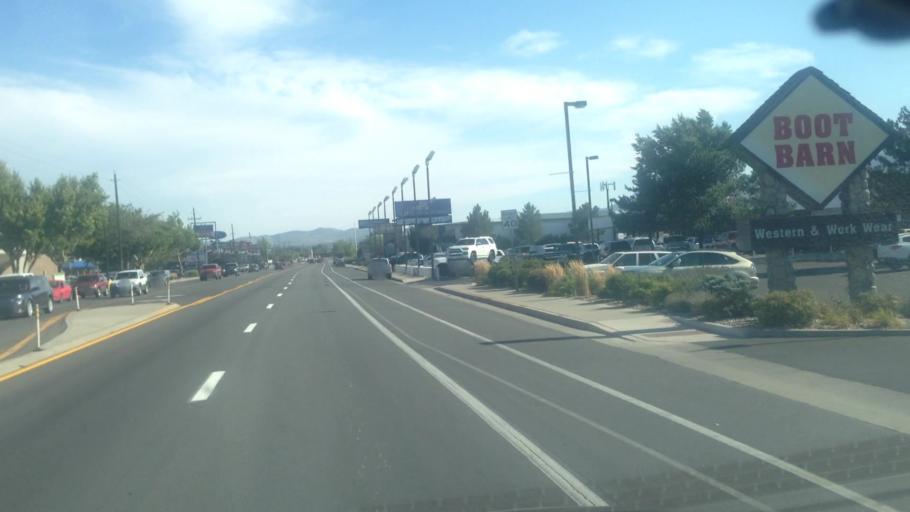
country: US
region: Nevada
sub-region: Washoe County
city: Reno
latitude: 39.4921
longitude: -119.7893
